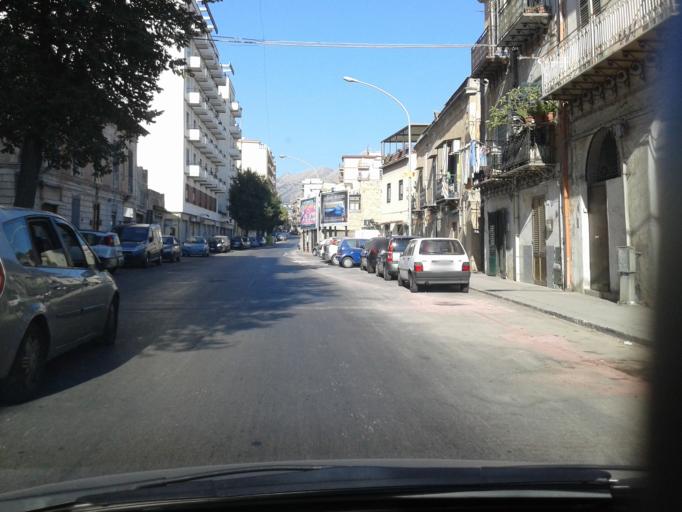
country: IT
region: Sicily
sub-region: Palermo
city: Palermo
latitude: 38.1108
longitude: 13.3441
